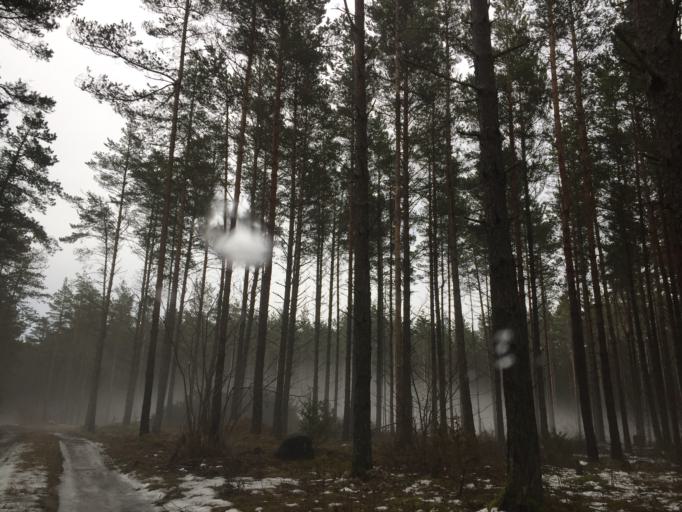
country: EE
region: Saare
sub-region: Orissaare vald
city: Orissaare
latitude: 58.6137
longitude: 22.9516
